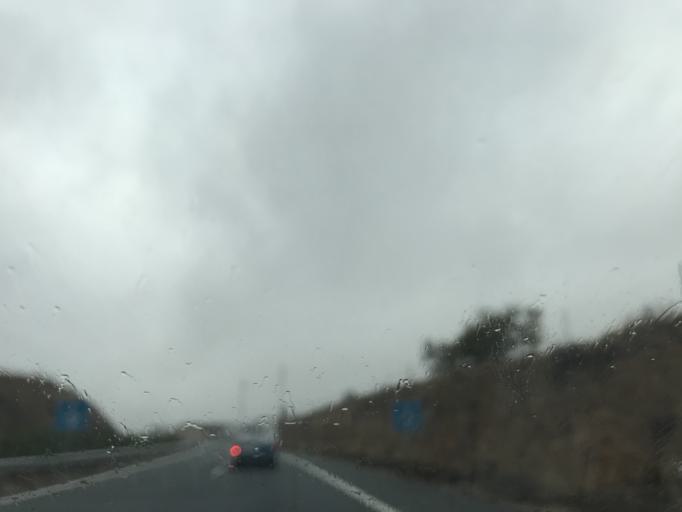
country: ES
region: Andalusia
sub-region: Provincia de Malaga
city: Mollina
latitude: 37.1134
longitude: -4.6597
